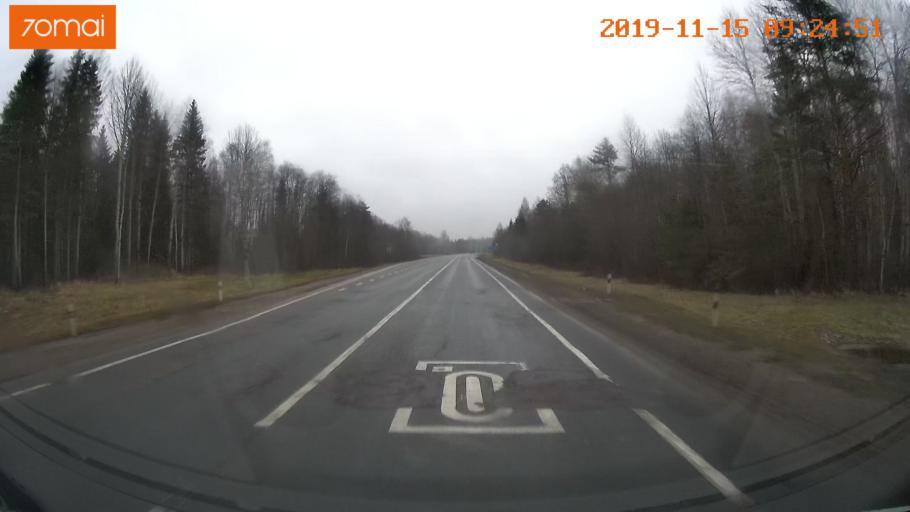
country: RU
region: Vologda
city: Tonshalovo
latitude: 59.3058
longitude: 38.1497
